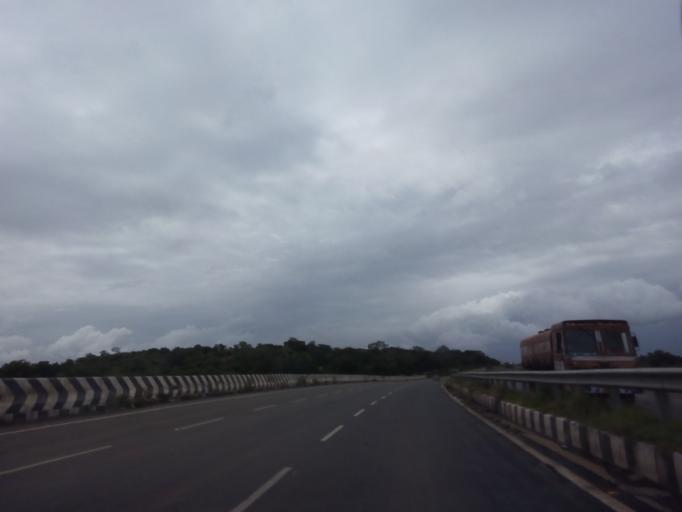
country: IN
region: Karnataka
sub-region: Haveri
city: Ranibennur
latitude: 14.5842
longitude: 75.6731
